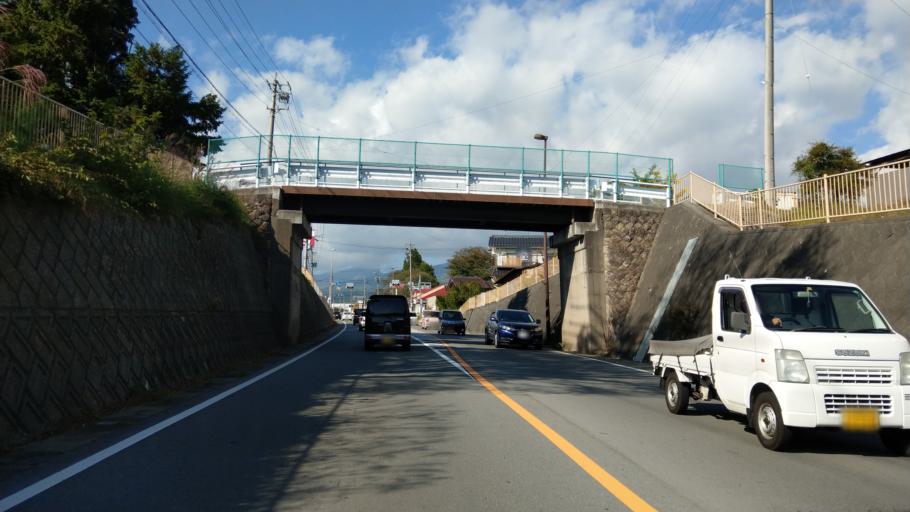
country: JP
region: Nagano
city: Komoro
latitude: 36.3243
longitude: 138.4360
